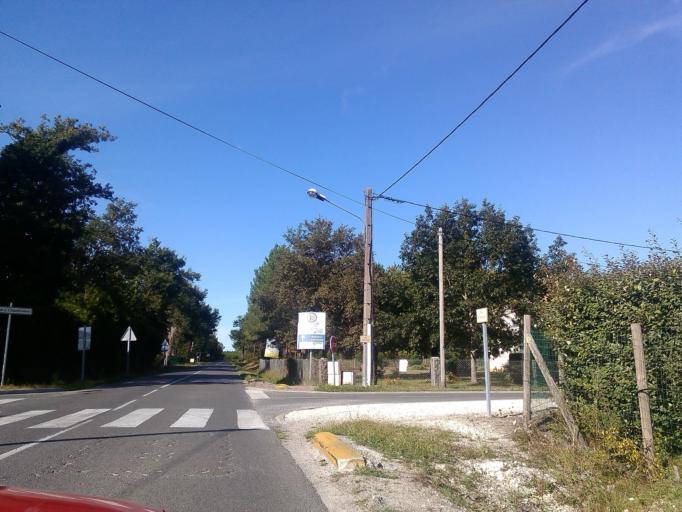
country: FR
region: Aquitaine
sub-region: Departement de la Gironde
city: Hourtin
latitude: 45.1897
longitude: -1.0537
